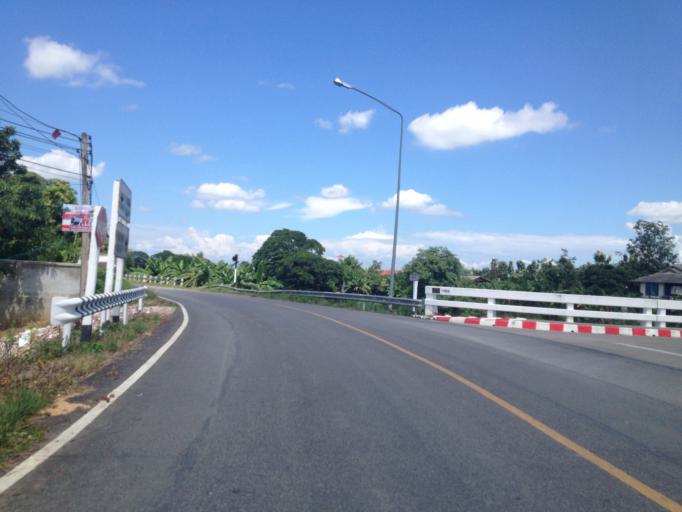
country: TH
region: Chiang Mai
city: Hang Dong
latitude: 18.6545
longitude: 98.9612
